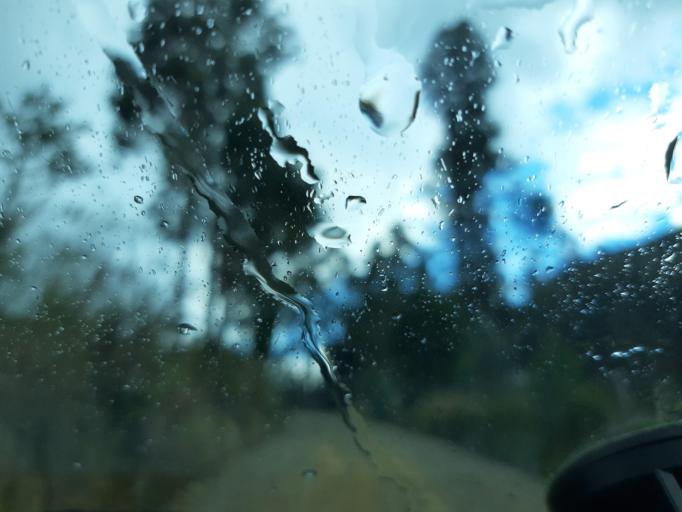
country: CO
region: Boyaca
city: Raquira
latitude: 5.4986
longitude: -73.6929
